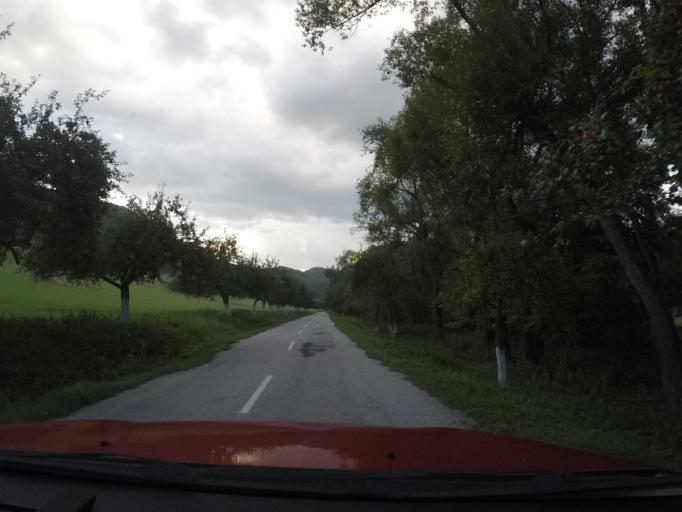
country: SK
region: Kosicky
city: Medzev
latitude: 48.6292
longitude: 20.7525
